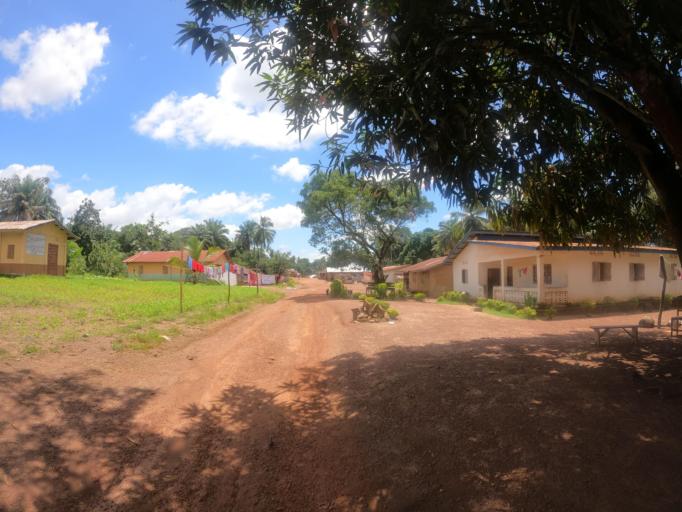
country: SL
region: Northern Province
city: Makeni
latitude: 8.8628
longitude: -12.1075
